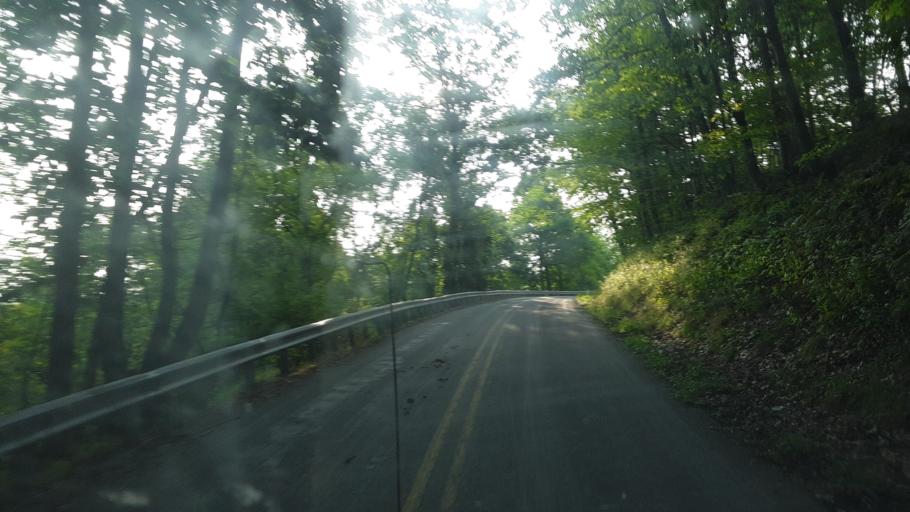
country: US
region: Pennsylvania
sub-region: Jefferson County
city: Punxsutawney
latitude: 40.9519
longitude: -79.1366
